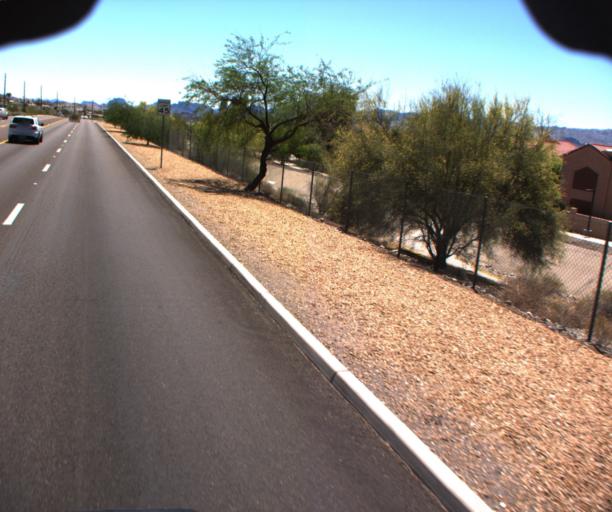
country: US
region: Arizona
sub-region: Mohave County
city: Lake Havasu City
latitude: 34.4676
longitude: -114.3390
